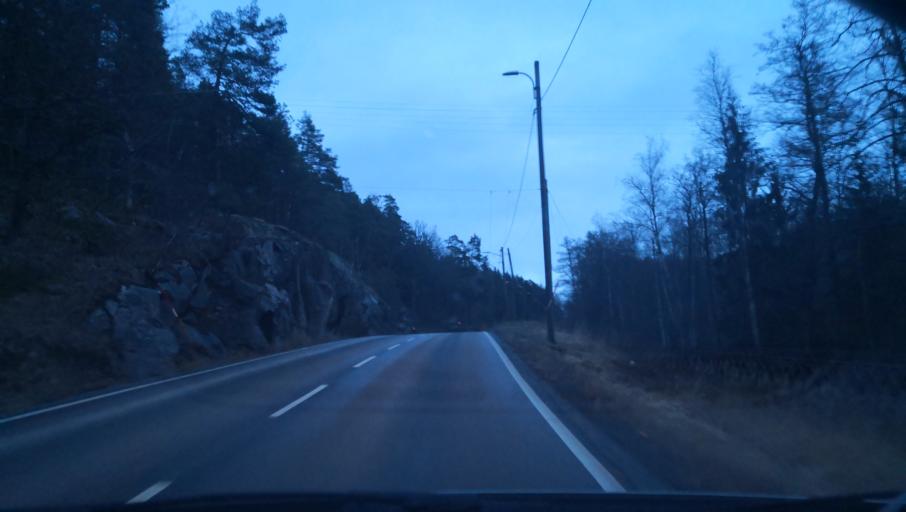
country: SE
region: Stockholm
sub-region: Varmdo Kommun
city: Gustavsberg
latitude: 59.3315
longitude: 18.3488
